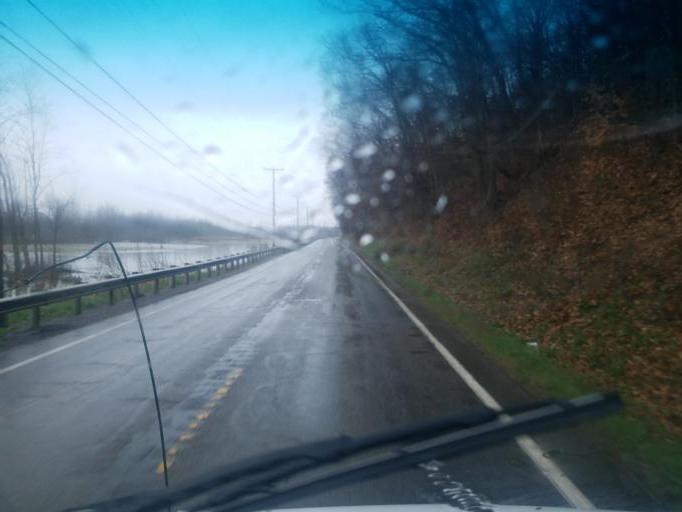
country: US
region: Ohio
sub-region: Holmes County
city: Millersburg
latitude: 40.5960
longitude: -81.9139
